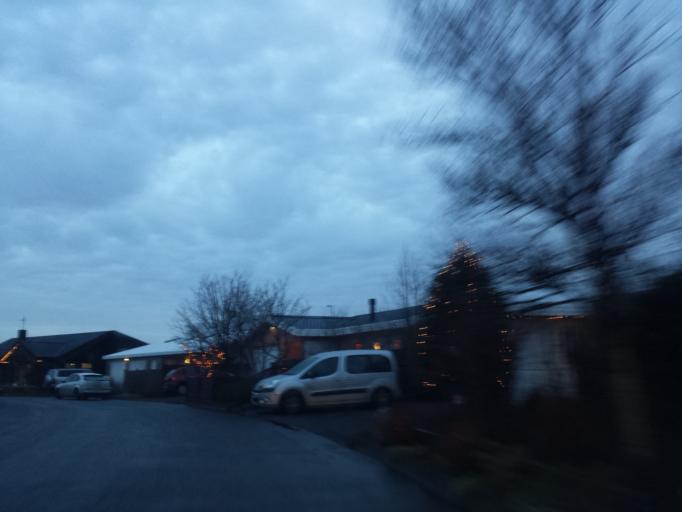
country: IS
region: Capital Region
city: Mosfellsbaer
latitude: 64.1368
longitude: -21.7726
